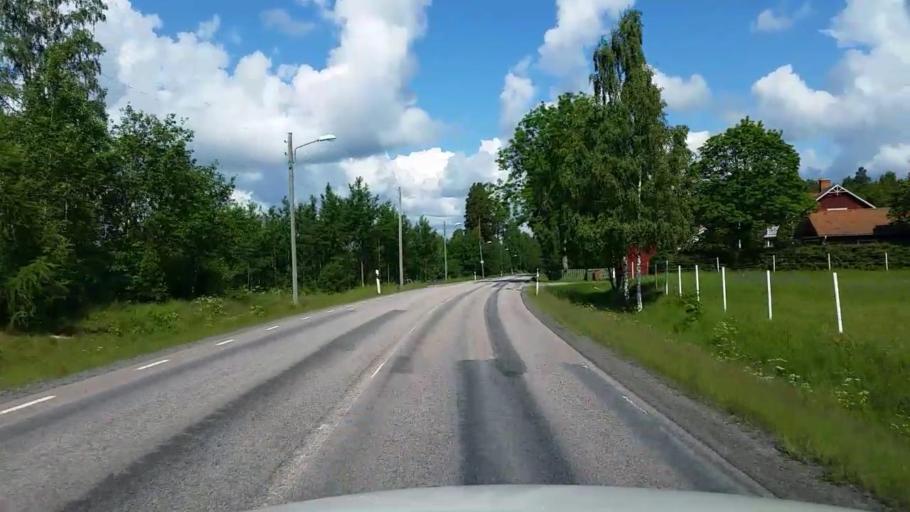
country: SE
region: Vaestmanland
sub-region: Kopings Kommun
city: Kolsva
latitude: 59.6292
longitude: 15.8066
